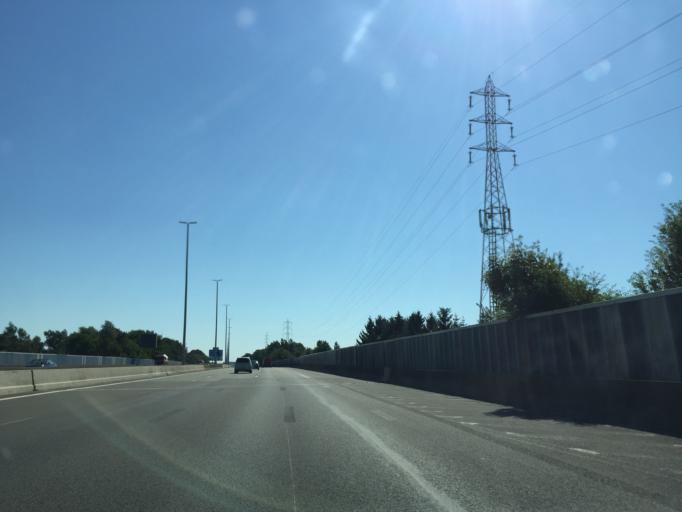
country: BE
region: Wallonia
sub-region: Province de Liege
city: Soumagne
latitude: 50.6342
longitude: 5.7583
